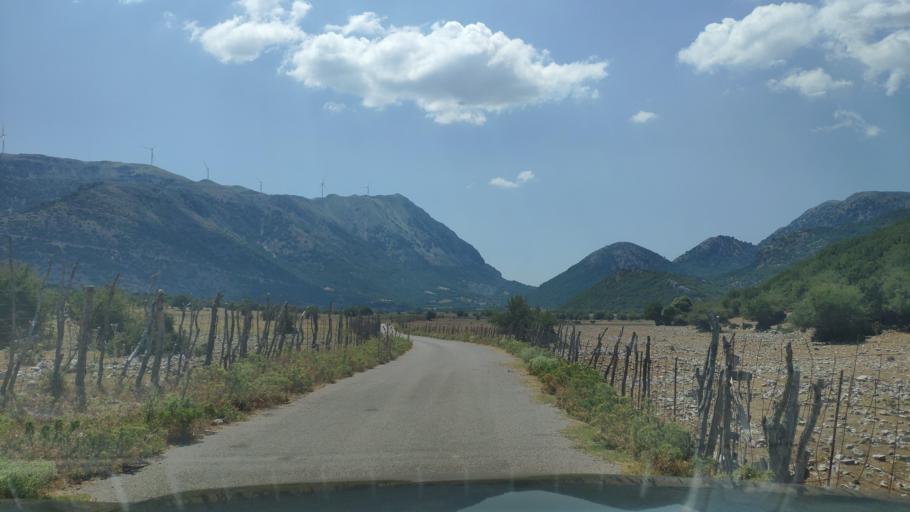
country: GR
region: West Greece
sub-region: Nomos Aitolias kai Akarnanias
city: Monastirakion
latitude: 38.7942
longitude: 20.9590
